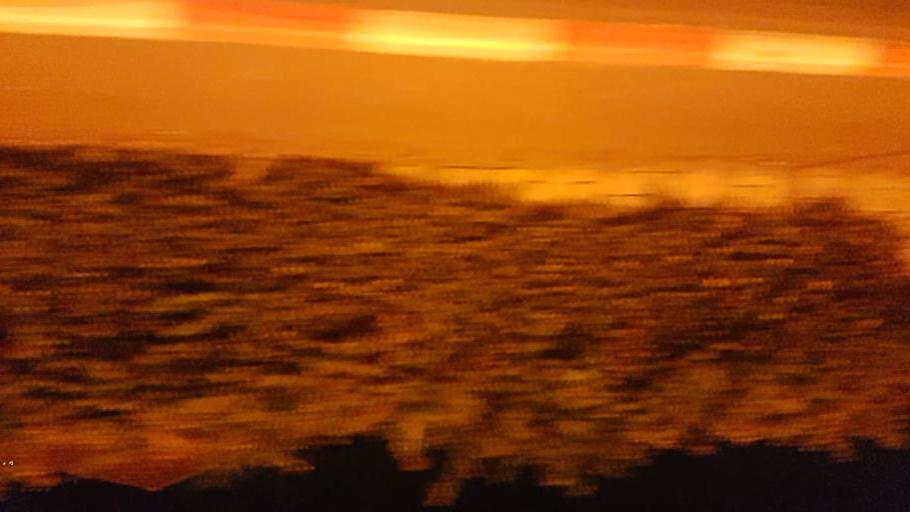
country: IL
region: Central District
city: Hod HaSharon
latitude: 32.1678
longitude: 34.8937
